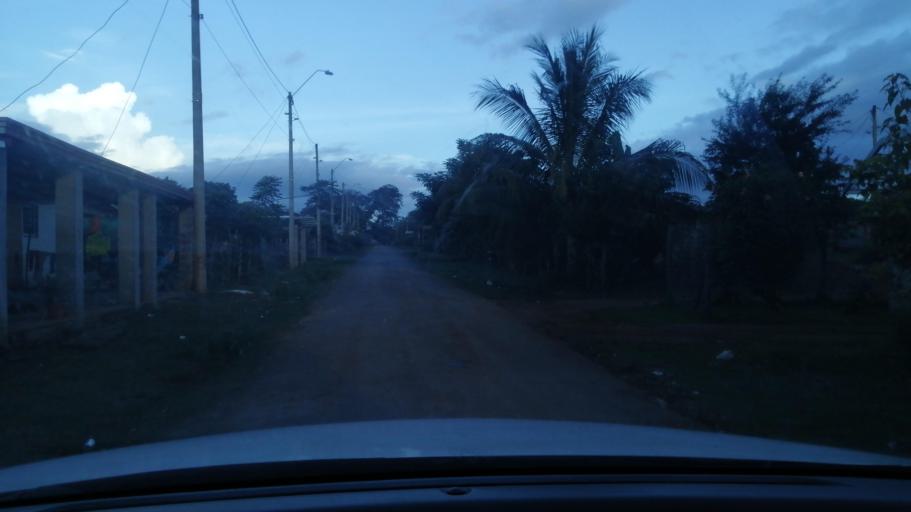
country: PA
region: Chiriqui
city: David
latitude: 8.4001
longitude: -82.4444
